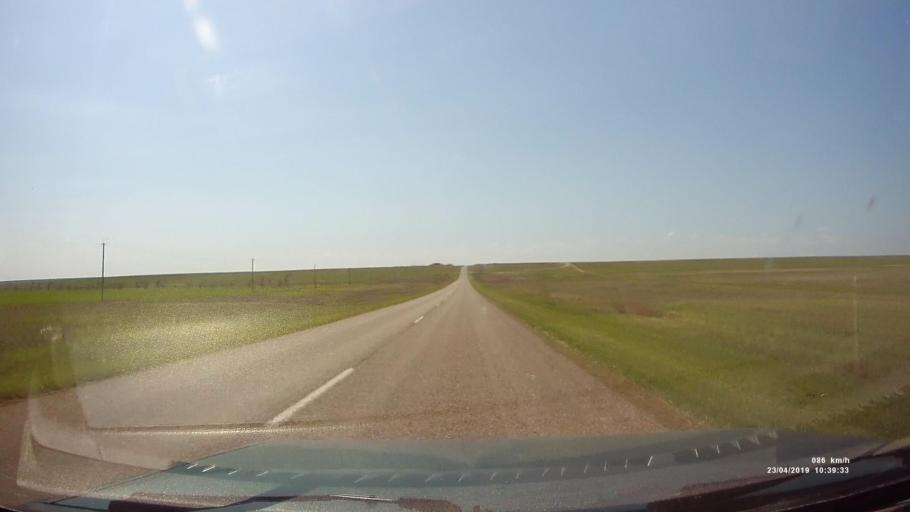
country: RU
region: Kalmykiya
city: Yashalta
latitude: 46.5178
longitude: 42.6387
